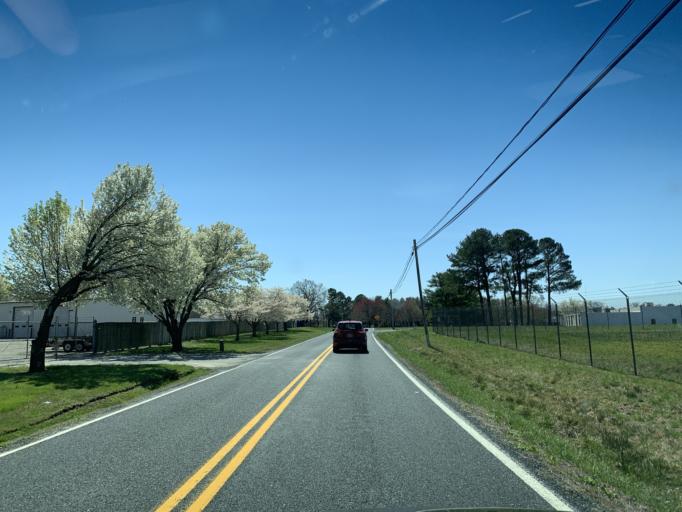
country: US
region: Maryland
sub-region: Talbot County
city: Easton
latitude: 38.7973
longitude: -76.0646
